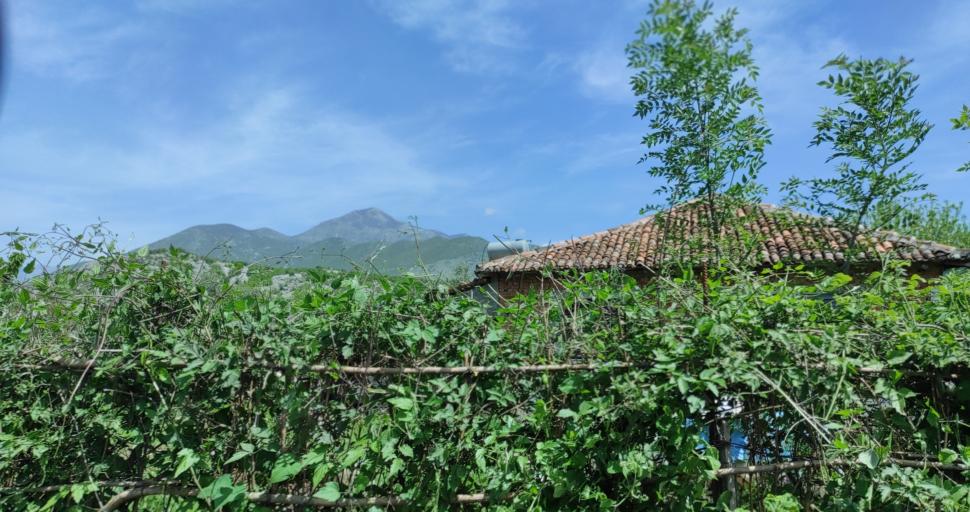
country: AL
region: Shkoder
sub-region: Rrethi i Malesia e Madhe
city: Gruemire
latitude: 42.1365
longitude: 19.5477
